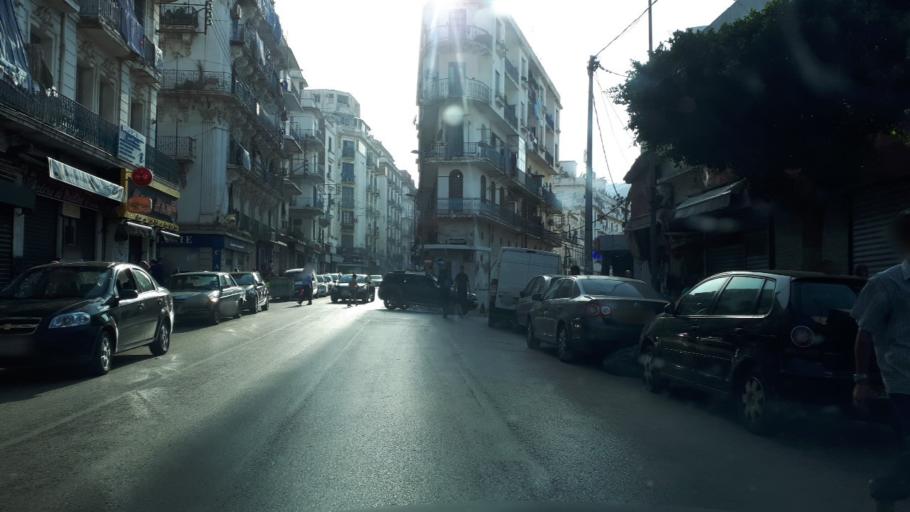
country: DZ
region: Alger
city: Algiers
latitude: 36.7912
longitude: 3.0559
